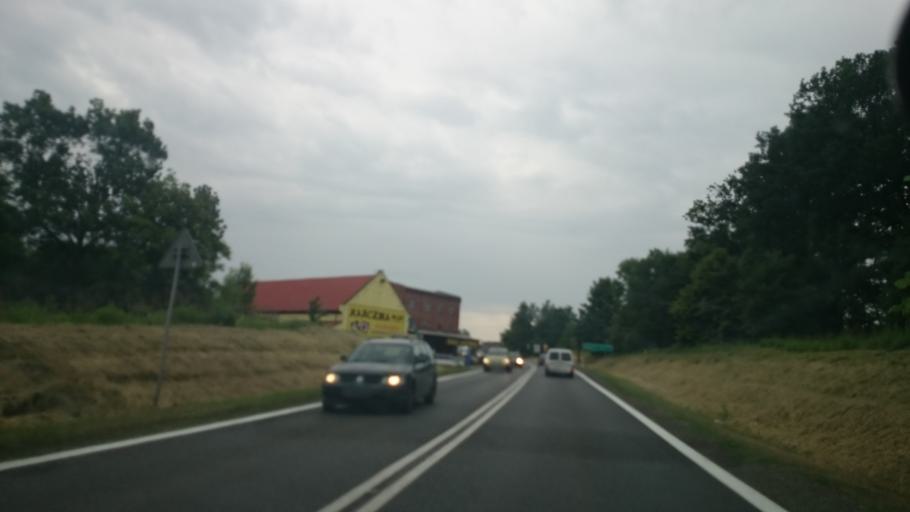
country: PL
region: Lower Silesian Voivodeship
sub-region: Powiat dzierzoniowski
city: Niemcza
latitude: 50.7376
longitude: 16.8385
